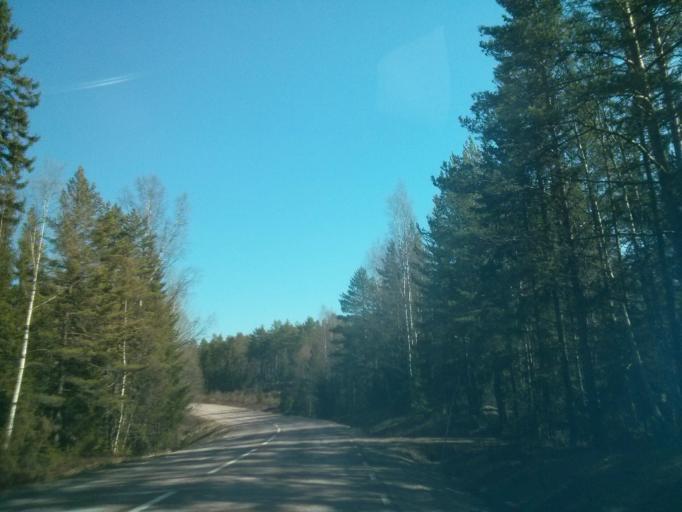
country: SE
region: Gaevleborg
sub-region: Hudiksvalls Kommun
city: Hudiksvall
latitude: 61.8477
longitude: 17.2749
